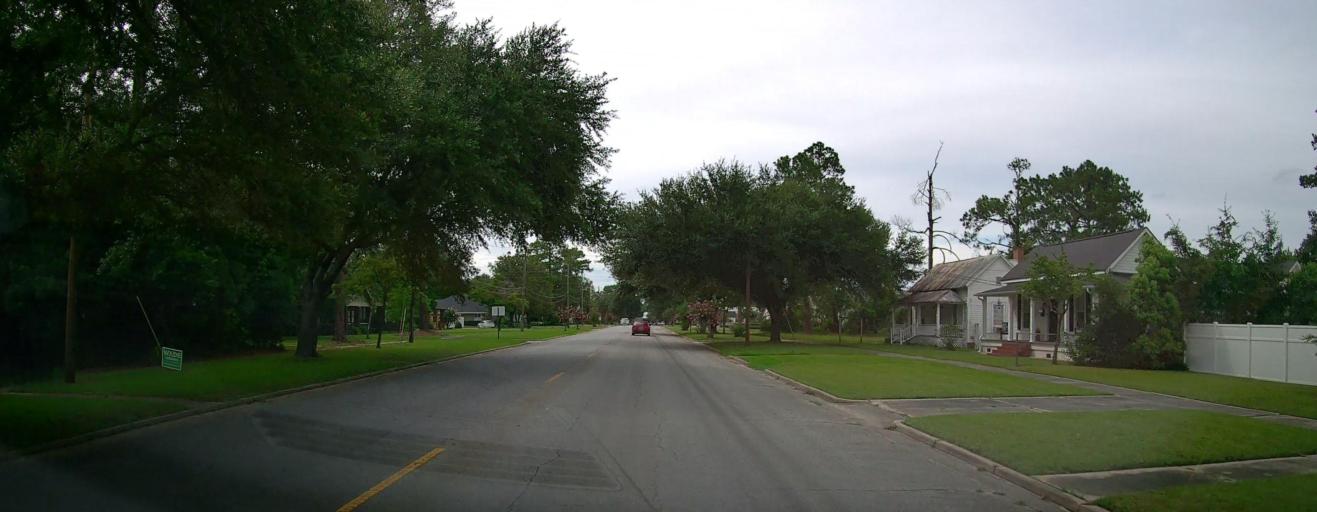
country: US
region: Georgia
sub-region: Wayne County
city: Jesup
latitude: 31.6000
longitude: -81.8766
